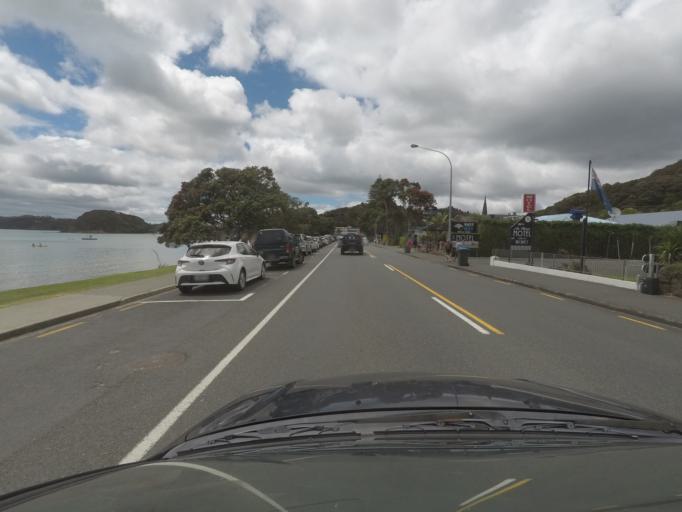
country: NZ
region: Northland
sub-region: Far North District
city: Paihia
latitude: -35.2828
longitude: 174.0933
